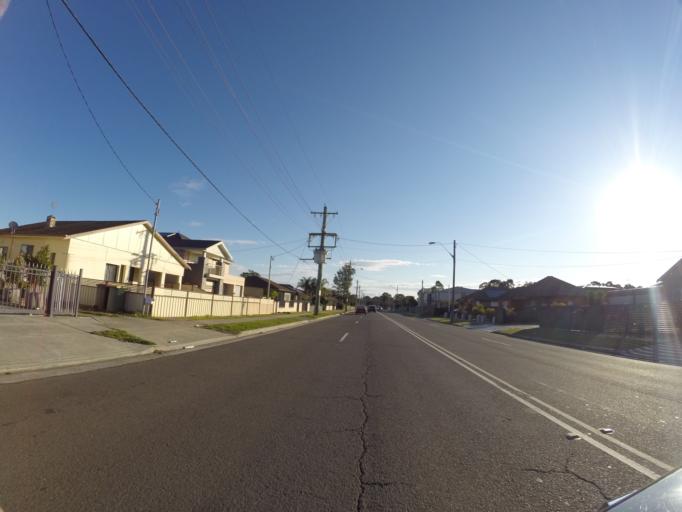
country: AU
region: New South Wales
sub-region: Fairfield
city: Fairfield East
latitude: -33.8685
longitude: 150.9689
